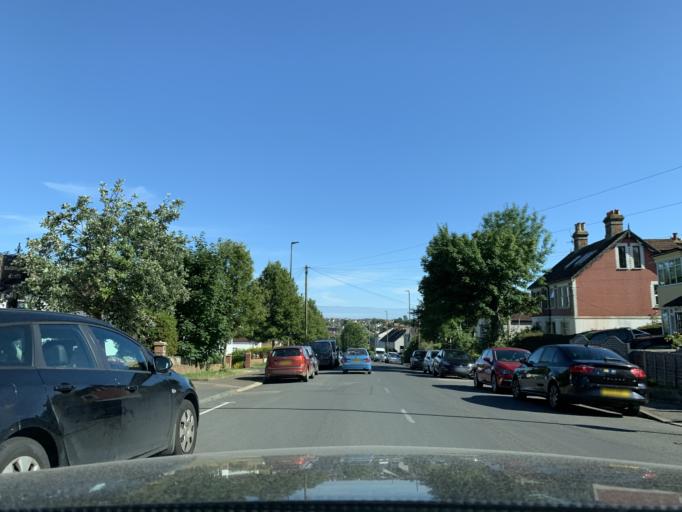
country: GB
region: England
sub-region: East Sussex
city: Saint Leonards-on-Sea
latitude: 50.8800
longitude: 0.5485
